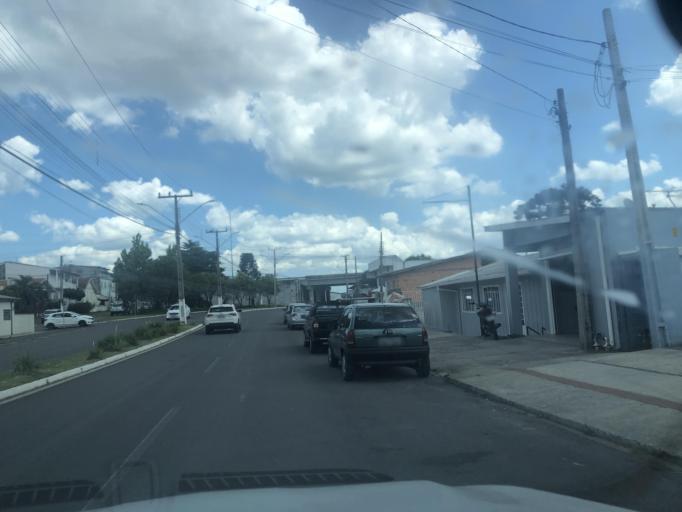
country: BR
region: Santa Catarina
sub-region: Lages
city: Lages
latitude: -27.7963
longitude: -50.3110
